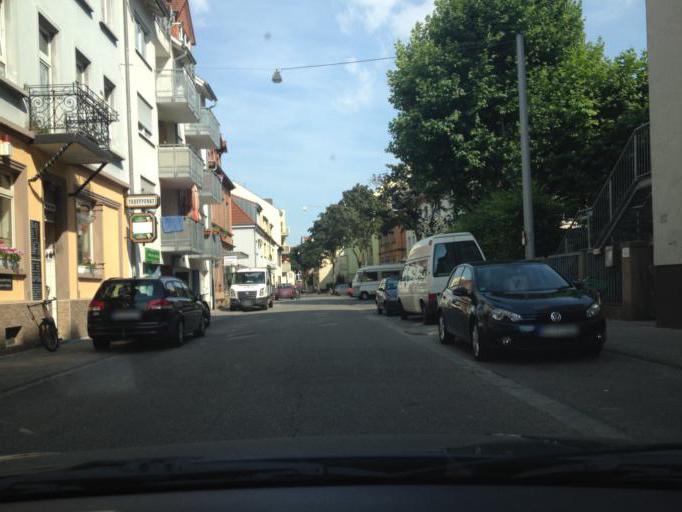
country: DE
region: Rheinland-Pfalz
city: Altrip
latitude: 49.4549
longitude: 8.4890
